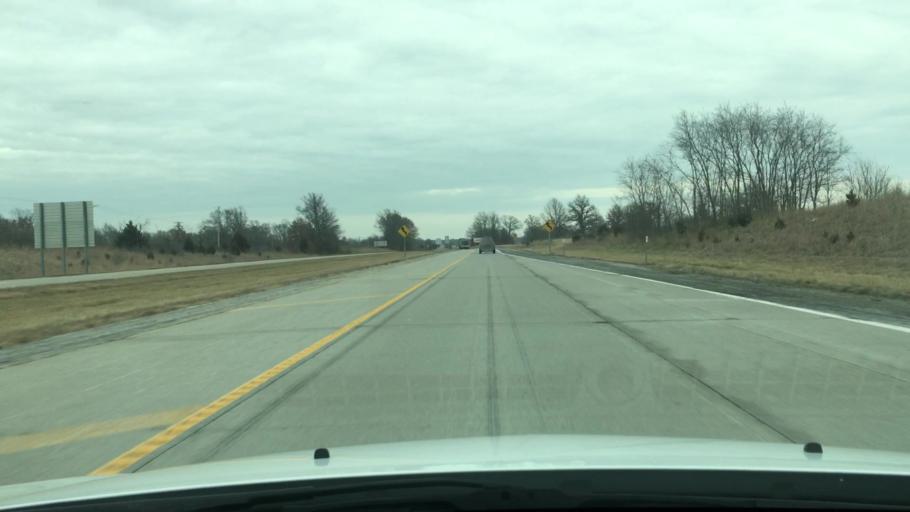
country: US
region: Missouri
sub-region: Audrain County
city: Mexico
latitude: 39.1194
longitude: -91.8854
